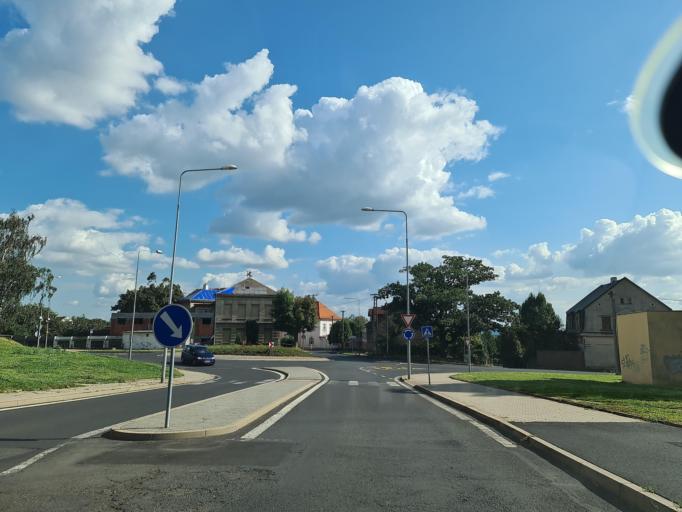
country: CZ
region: Ustecky
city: Horni Jiretin
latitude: 50.5927
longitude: 13.5727
